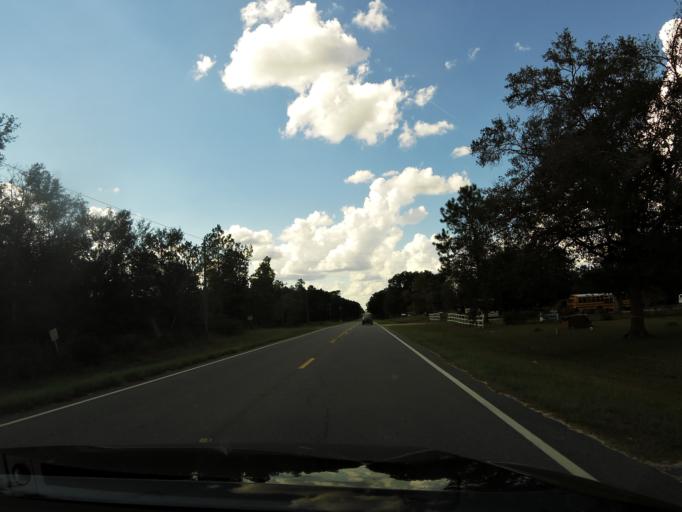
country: US
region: Georgia
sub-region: Lowndes County
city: Valdosta
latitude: 30.7769
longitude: -83.1514
